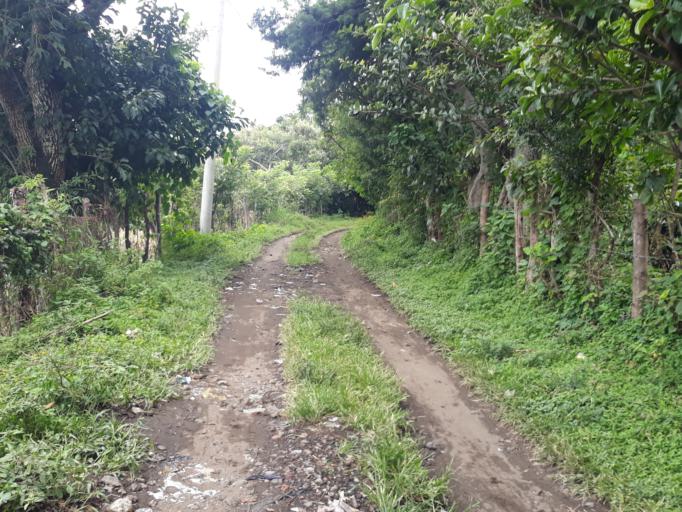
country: GT
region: Escuintla
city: San Vicente Pacaya
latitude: 14.3681
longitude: -90.5536
